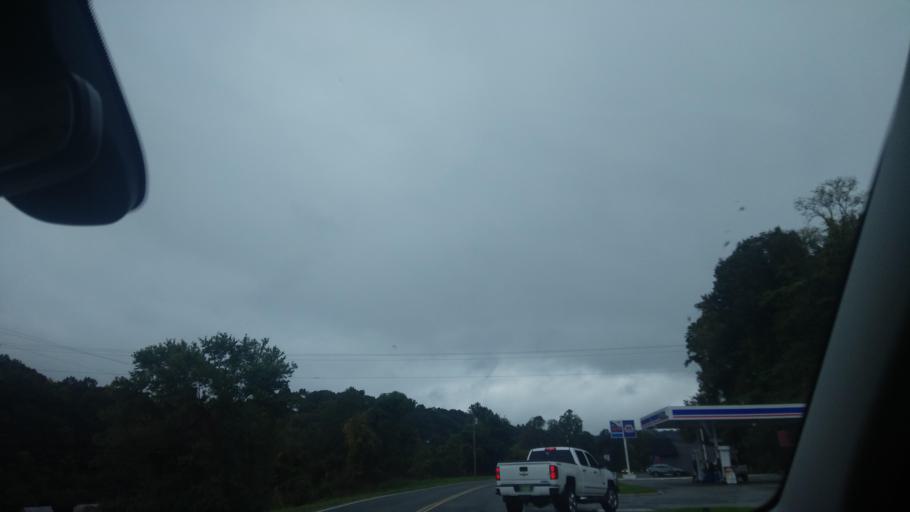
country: US
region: Virginia
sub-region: City of Galax
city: Galax
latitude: 36.6529
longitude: -80.9190
